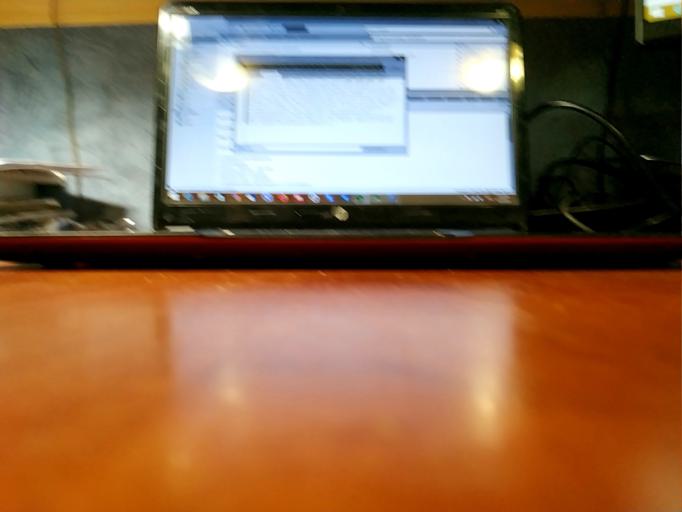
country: RU
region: Tverskaya
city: Sandovo
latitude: 58.5758
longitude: 36.4136
